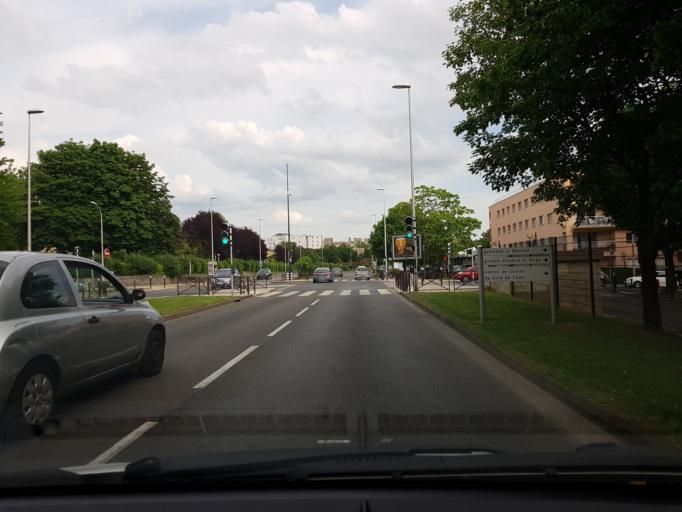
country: FR
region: Ile-de-France
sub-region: Departement de Seine-et-Marne
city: Torcy
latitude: 48.8445
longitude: 2.6488
